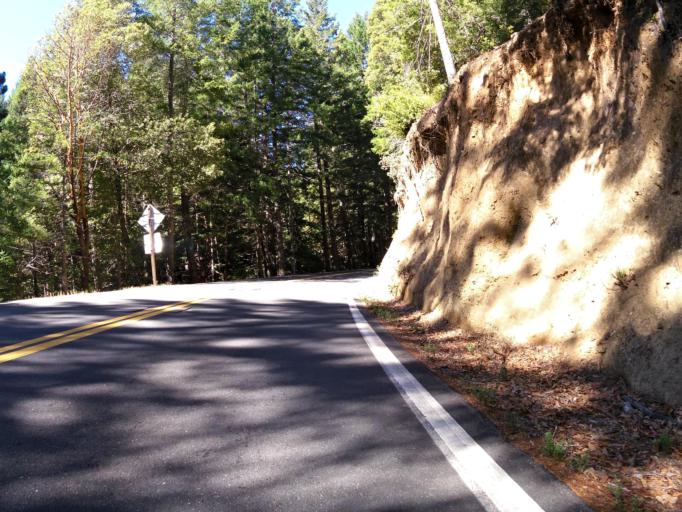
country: US
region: California
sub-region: Humboldt County
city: Redway
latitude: 39.8501
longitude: -123.7302
